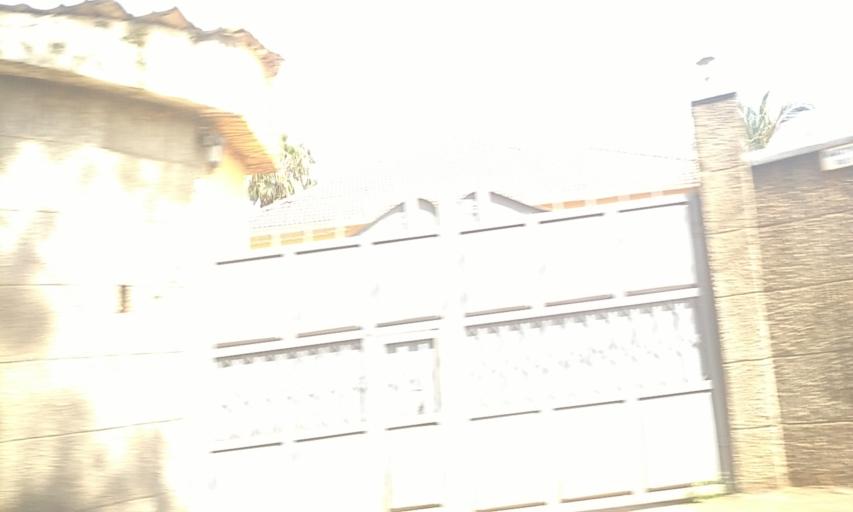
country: UG
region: Central Region
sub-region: Wakiso District
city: Kireka
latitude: 0.3555
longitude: 32.6177
